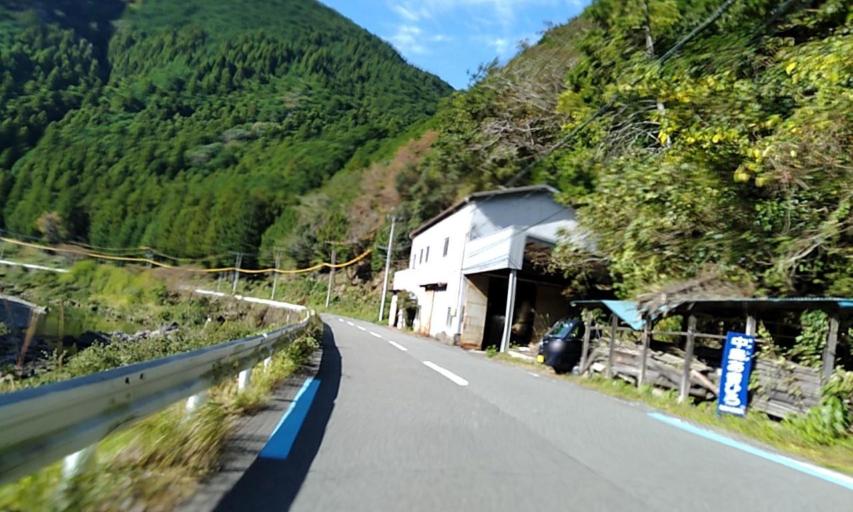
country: JP
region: Wakayama
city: Kainan
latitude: 34.0620
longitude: 135.3526
